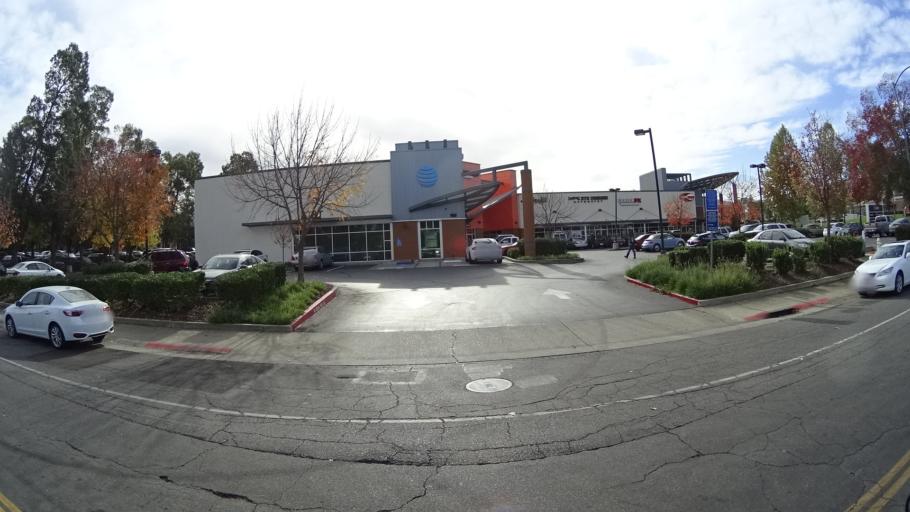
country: US
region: California
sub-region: Sacramento County
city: Fair Oaks
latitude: 38.6681
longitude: -121.2713
